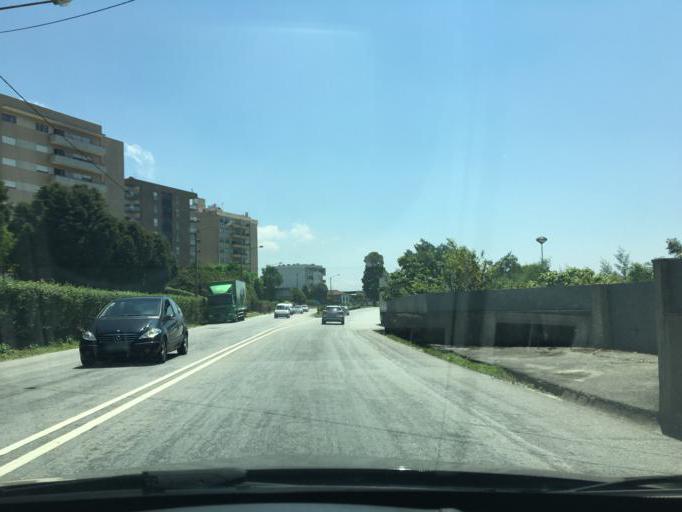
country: PT
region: Porto
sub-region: Maia
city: Gemunde
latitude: 41.2506
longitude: -8.6504
